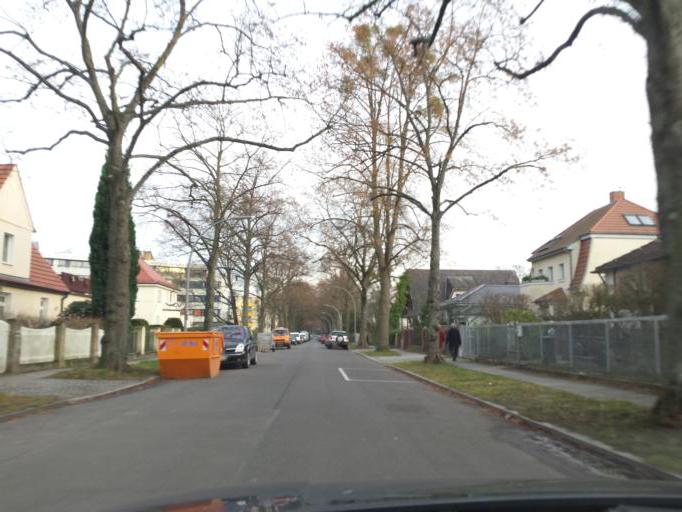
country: DE
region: Berlin
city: Zehlendorf Bezirk
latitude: 52.4337
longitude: 13.2676
